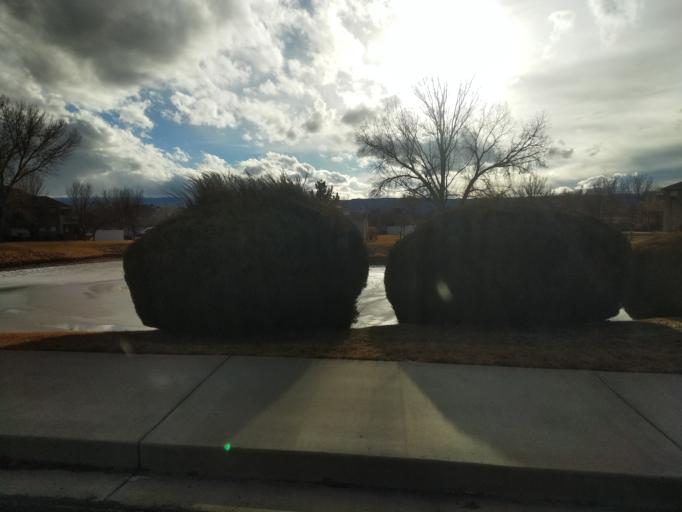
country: US
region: Colorado
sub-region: Mesa County
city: Redlands
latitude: 39.1104
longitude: -108.5912
